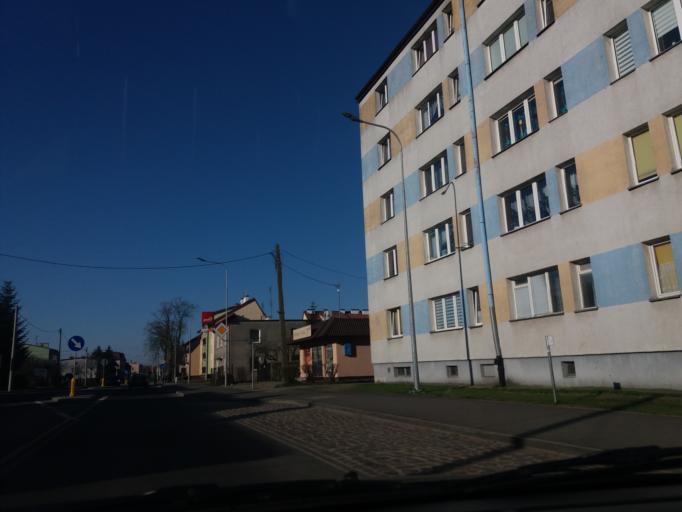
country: PL
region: Warmian-Masurian Voivodeship
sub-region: Powiat nidzicki
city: Nidzica
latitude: 53.3642
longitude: 20.4274
